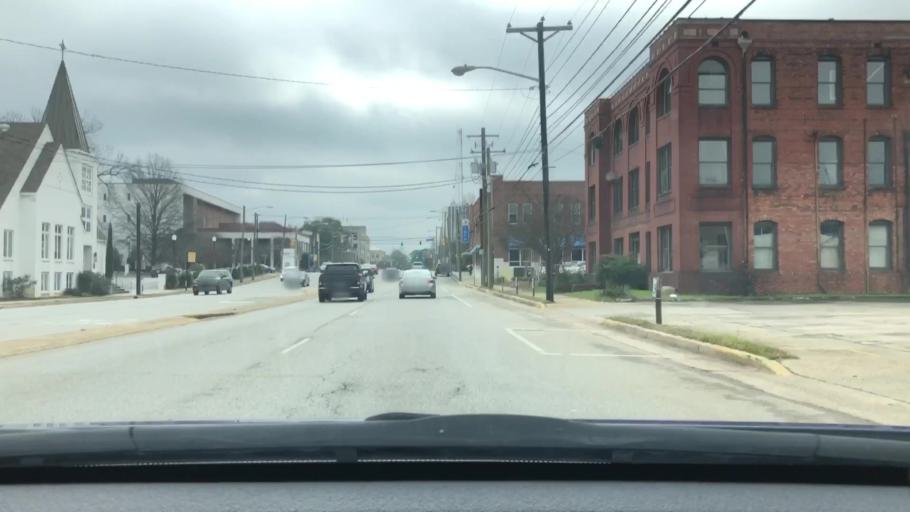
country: US
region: South Carolina
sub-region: Richland County
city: Columbia
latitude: 34.0079
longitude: -81.0311
